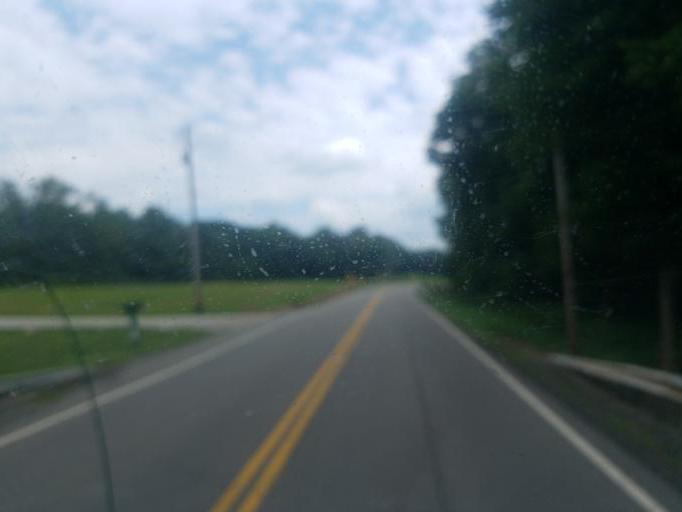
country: US
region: Ohio
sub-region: Licking County
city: Utica
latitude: 40.1605
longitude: -82.4602
